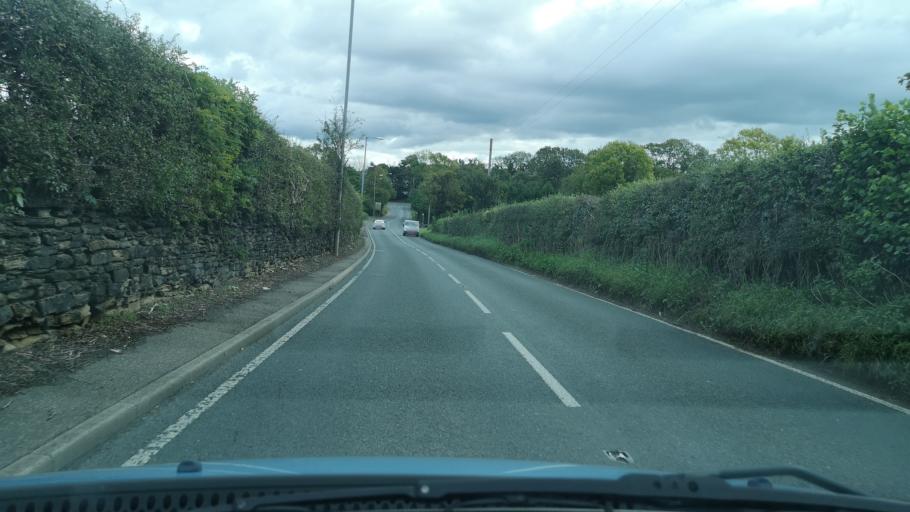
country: GB
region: England
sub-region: City and Borough of Wakefield
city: Middlestown
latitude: 53.6573
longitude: -1.5849
